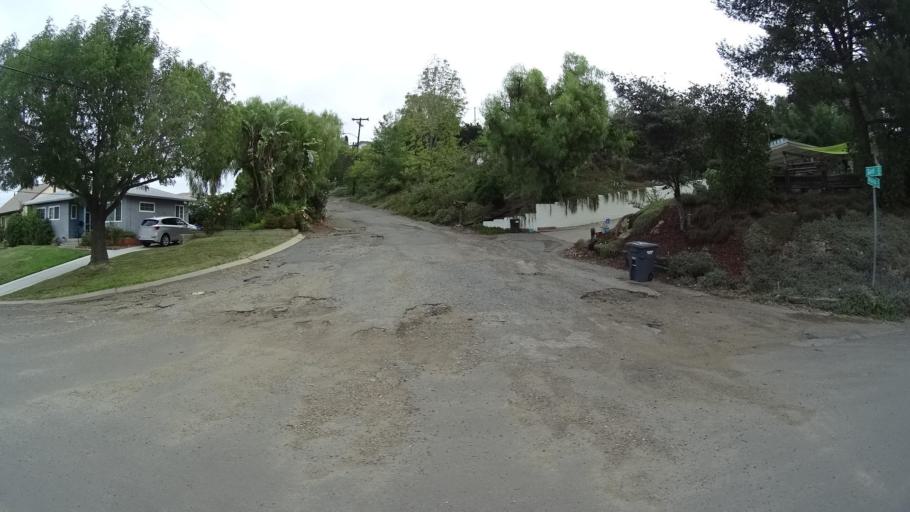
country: US
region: California
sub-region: San Diego County
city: Spring Valley
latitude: 32.7439
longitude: -117.0138
